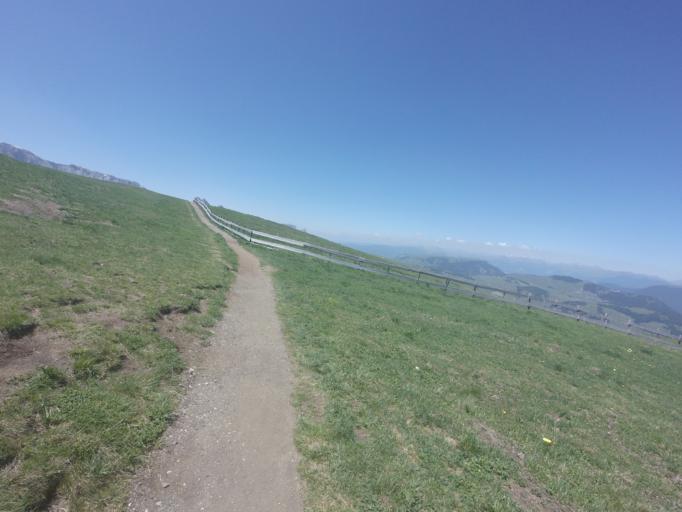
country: IT
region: Trentino-Alto Adige
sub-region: Provincia di Trento
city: Mazzin
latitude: 46.5043
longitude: 11.6994
